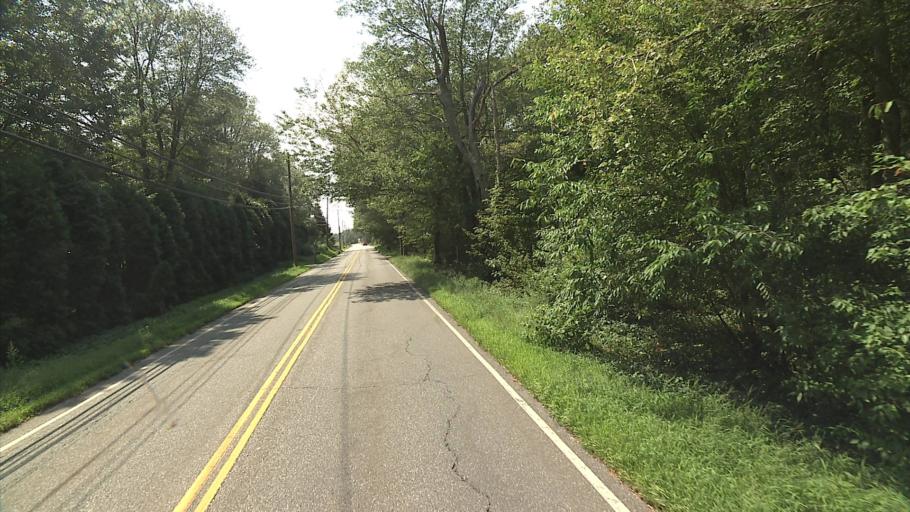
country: US
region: Connecticut
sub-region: New London County
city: Montville Center
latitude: 41.5000
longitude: -72.2197
